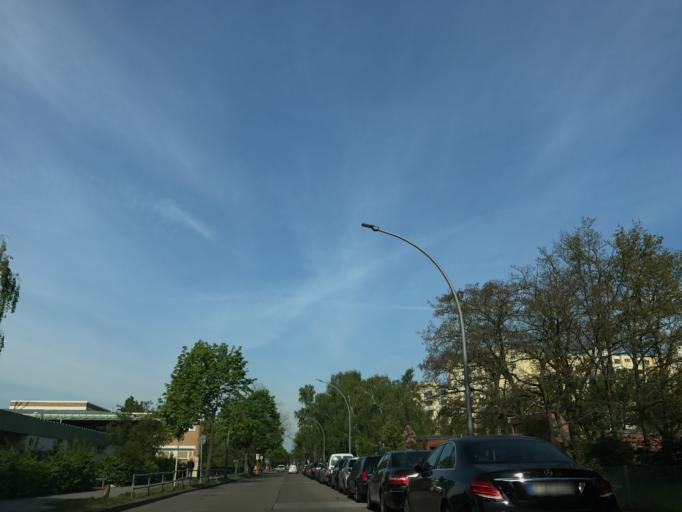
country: DE
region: Berlin
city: Falkenhagener Feld
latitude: 52.5488
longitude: 13.1586
